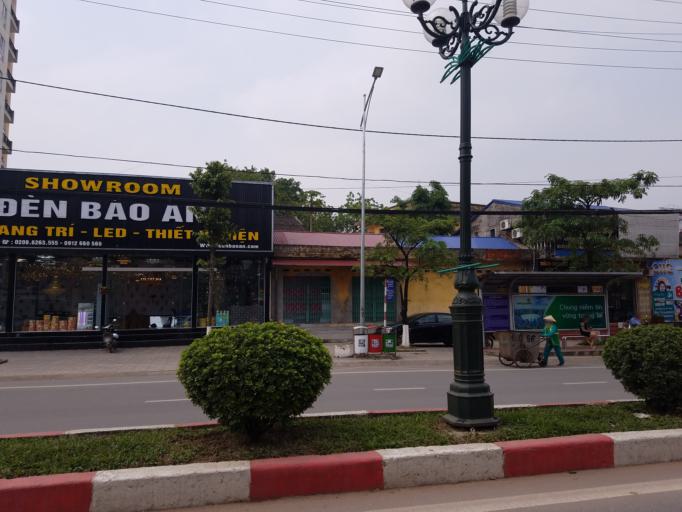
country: VN
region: Thai Nguyen
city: Thanh Pho Thai Nguyen
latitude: 21.5878
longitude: 105.8280
